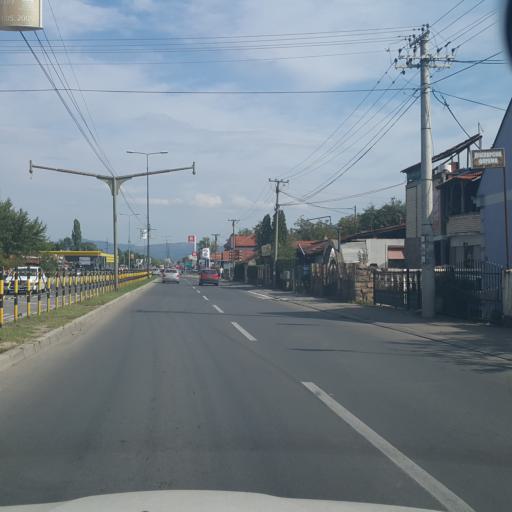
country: RS
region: Central Serbia
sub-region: Nisavski Okrug
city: Nis
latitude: 43.3107
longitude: 21.9326
